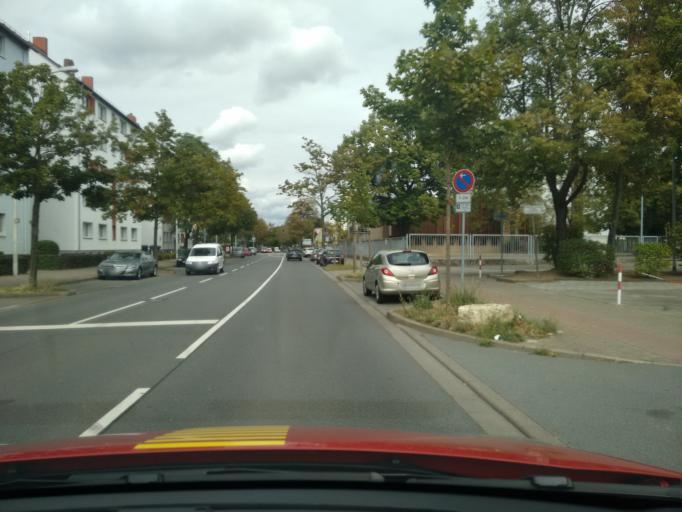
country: DE
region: Rheinland-Pfalz
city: Mainz
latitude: 49.9878
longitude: 8.2677
